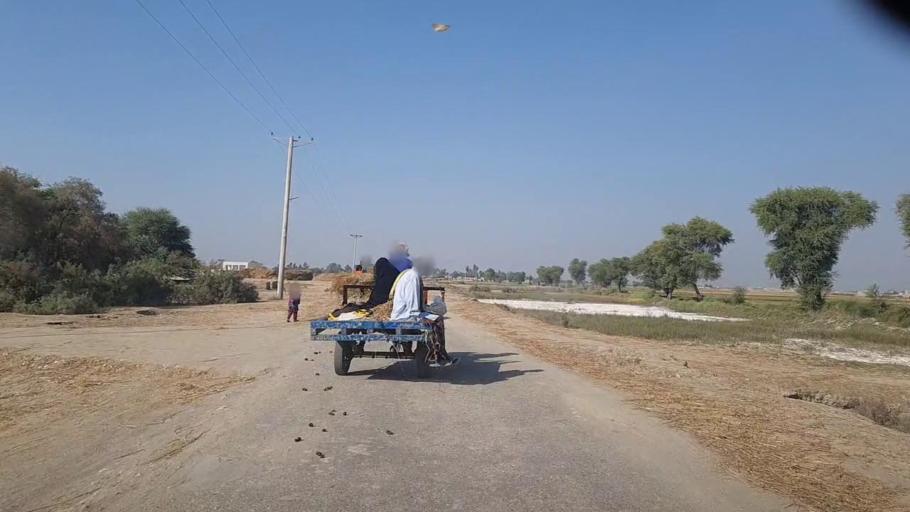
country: PK
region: Sindh
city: Tangwani
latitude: 28.2480
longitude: 68.9960
